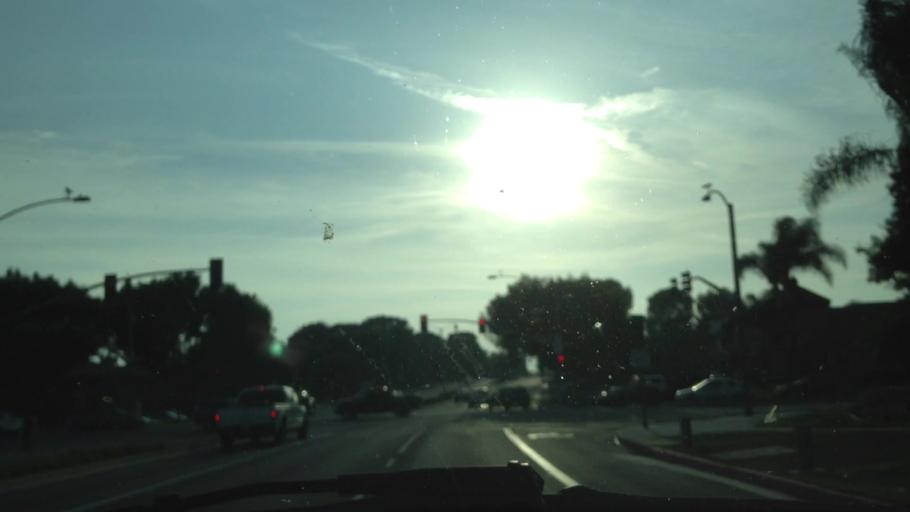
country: US
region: California
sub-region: Orange County
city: Placentia
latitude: 33.8711
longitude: -117.8621
